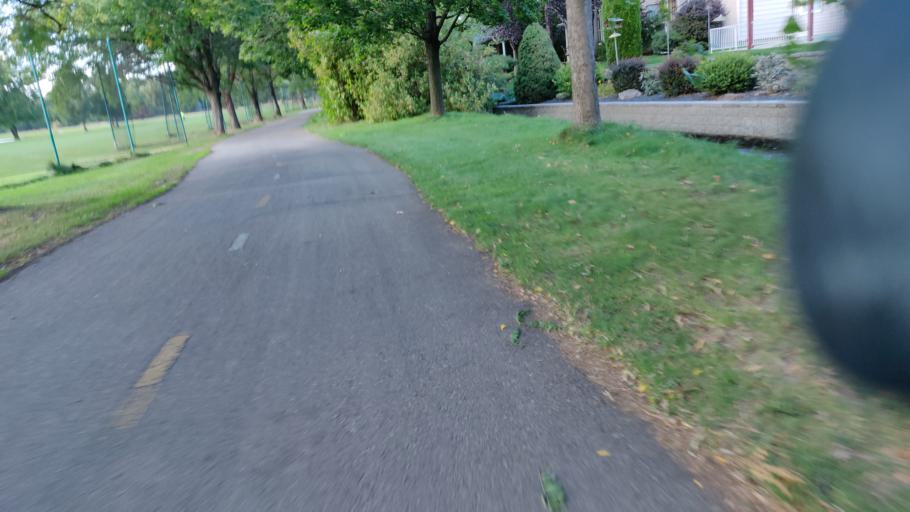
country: US
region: Idaho
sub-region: Ada County
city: Boise
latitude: 43.5979
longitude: -116.1702
